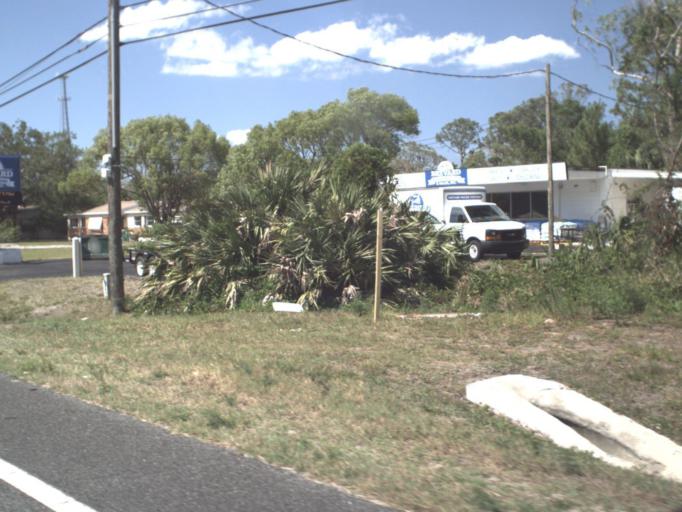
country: US
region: Florida
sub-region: Brevard County
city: Mims
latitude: 28.6844
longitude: -80.8537
